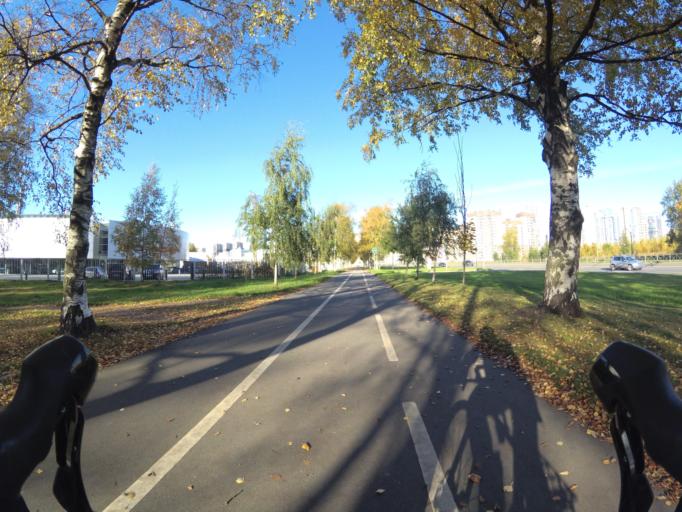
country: RU
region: Leningrad
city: Untolovo
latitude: 59.9924
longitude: 30.2164
